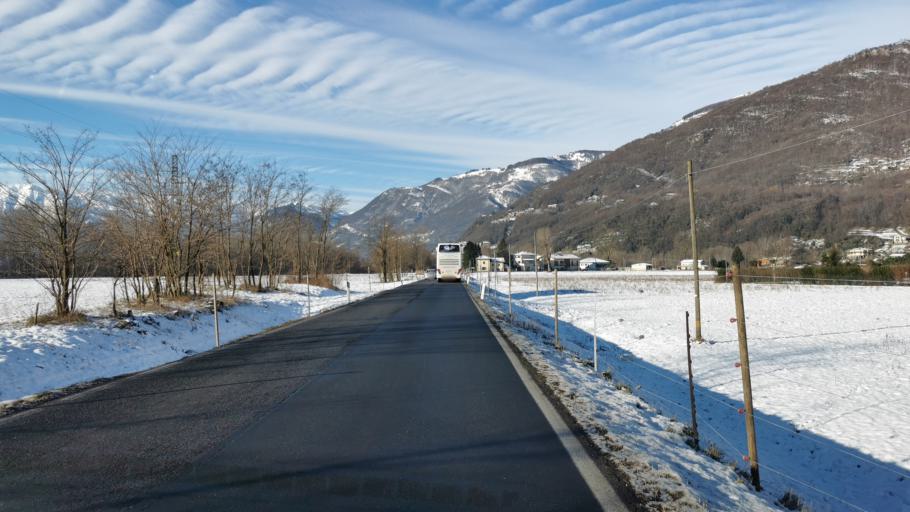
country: IT
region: Lombardy
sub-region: Provincia di Sondrio
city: Dubino
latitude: 46.1720
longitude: 9.4189
